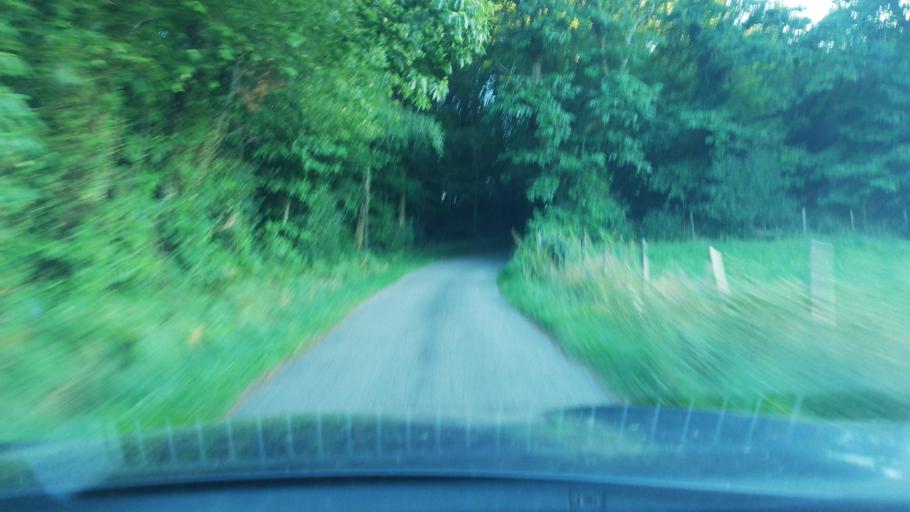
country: FR
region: Midi-Pyrenees
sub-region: Departement du Lot
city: Saint-Cere
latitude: 44.8771
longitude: 1.9951
